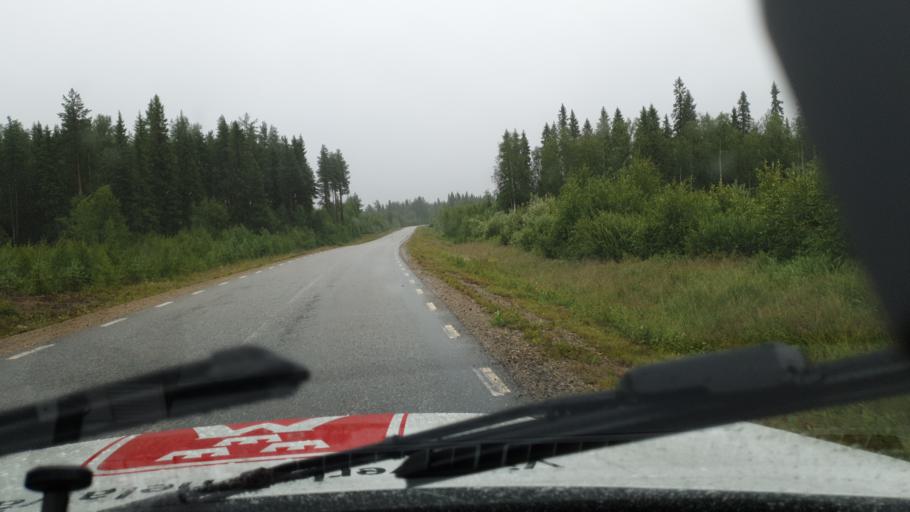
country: SE
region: Vaesterbotten
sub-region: Skelleftea Kommun
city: Langsele
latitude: 64.6404
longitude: 19.9872
